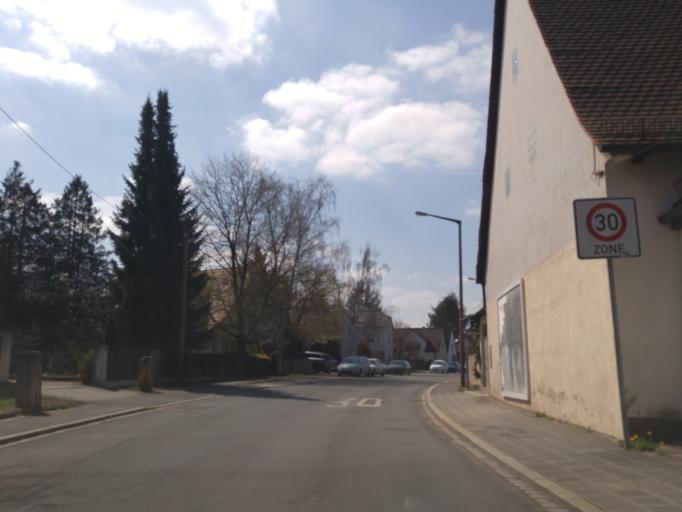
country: DE
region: Bavaria
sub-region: Regierungsbezirk Mittelfranken
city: Wetzendorf
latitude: 49.4711
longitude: 11.0367
